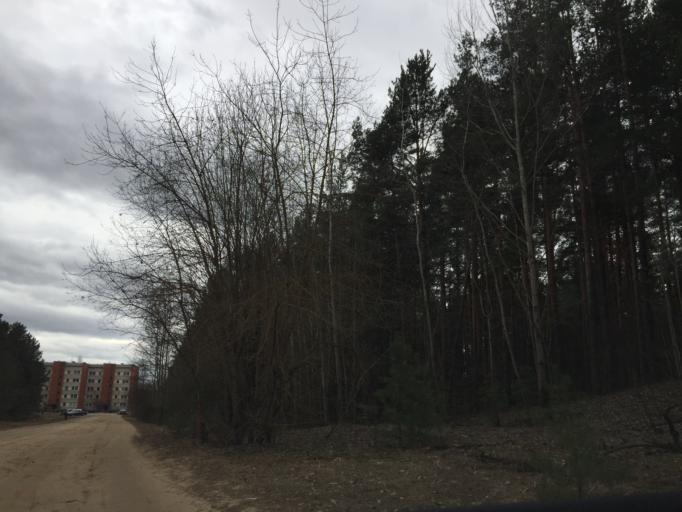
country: LV
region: Daugavpils
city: Daugavpils
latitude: 55.9071
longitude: 26.5377
